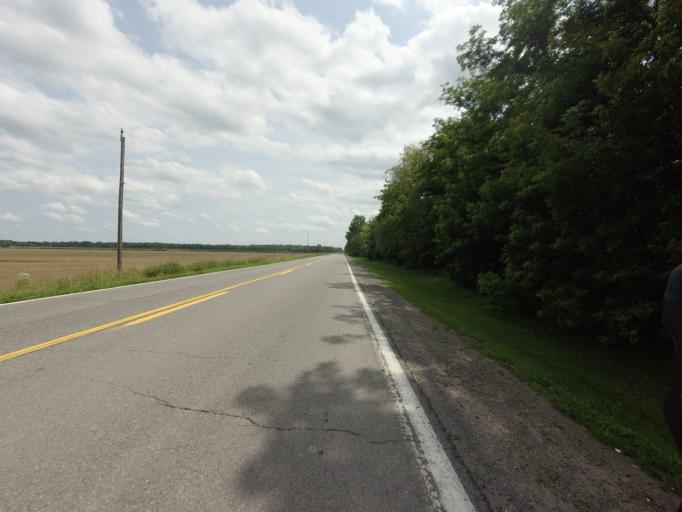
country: CA
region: Ontario
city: Ottawa
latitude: 45.1965
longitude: -75.5893
